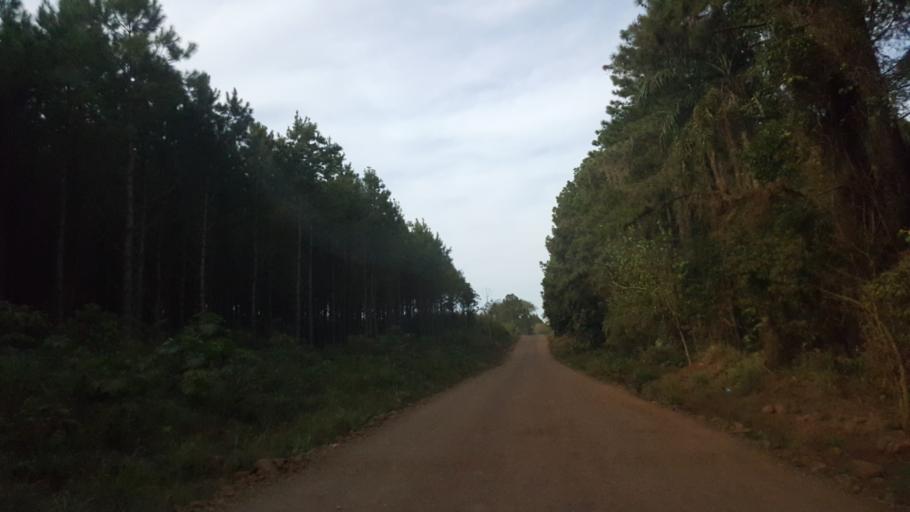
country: AR
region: Misiones
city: Capiovi
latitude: -26.9303
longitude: -55.1160
